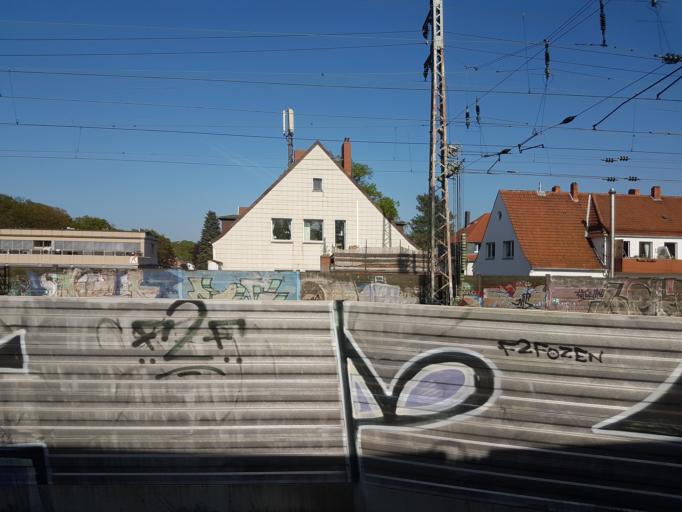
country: DE
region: Lower Saxony
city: Laatzen
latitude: 52.3501
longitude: 9.7731
